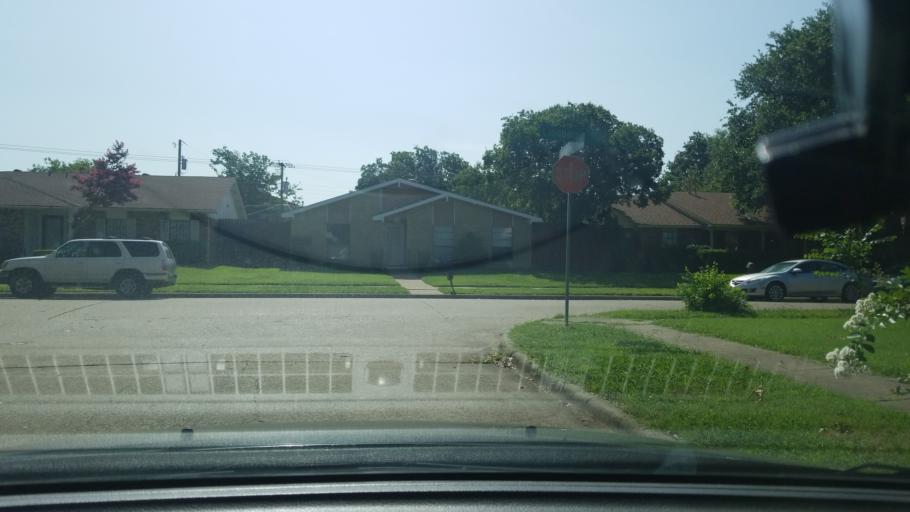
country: US
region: Texas
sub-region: Dallas County
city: Mesquite
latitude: 32.8019
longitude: -96.6918
